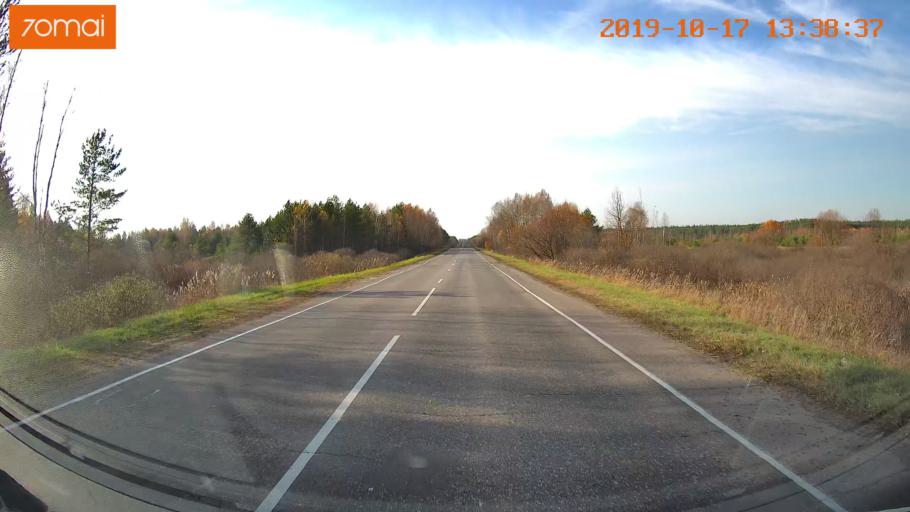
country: RU
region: Rjazan
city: Tuma
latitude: 55.1443
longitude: 40.6091
